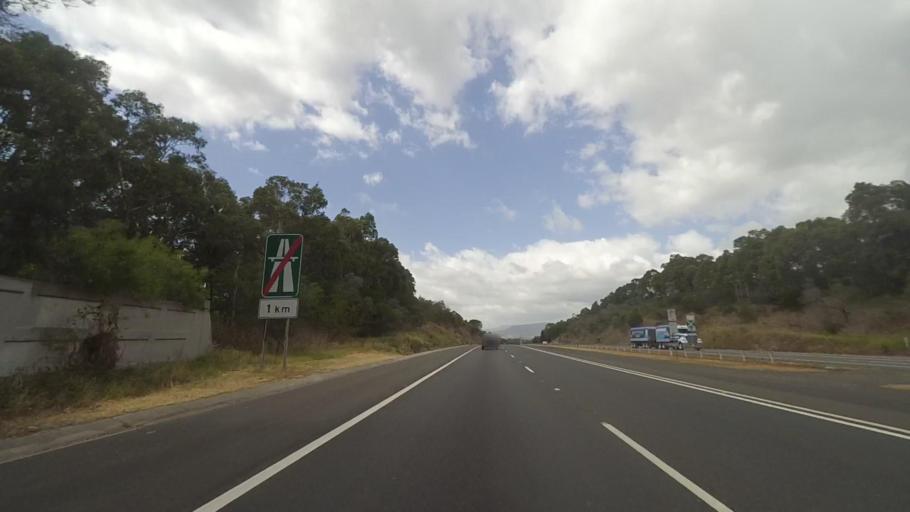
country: AU
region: New South Wales
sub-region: Wollongong
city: Dapto
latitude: -34.5173
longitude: 150.7894
